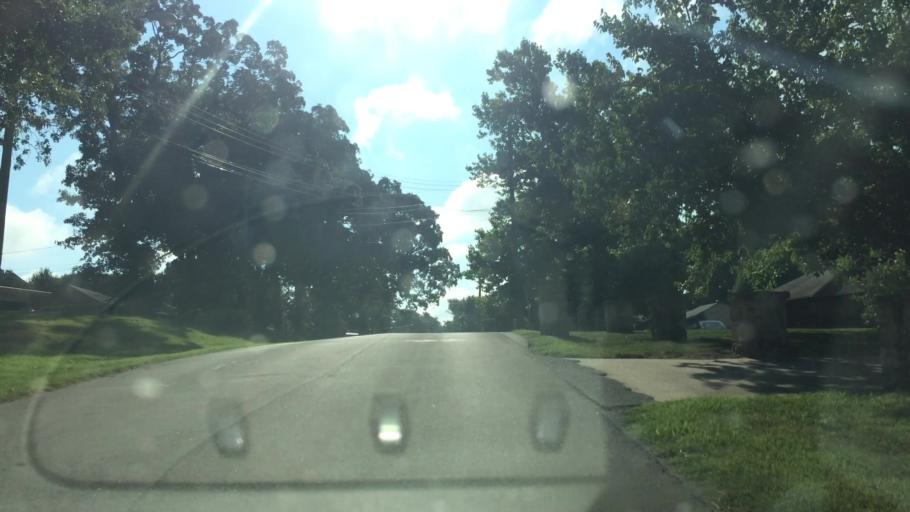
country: US
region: Missouri
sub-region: Greene County
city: Springfield
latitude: 37.2595
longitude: -93.2784
